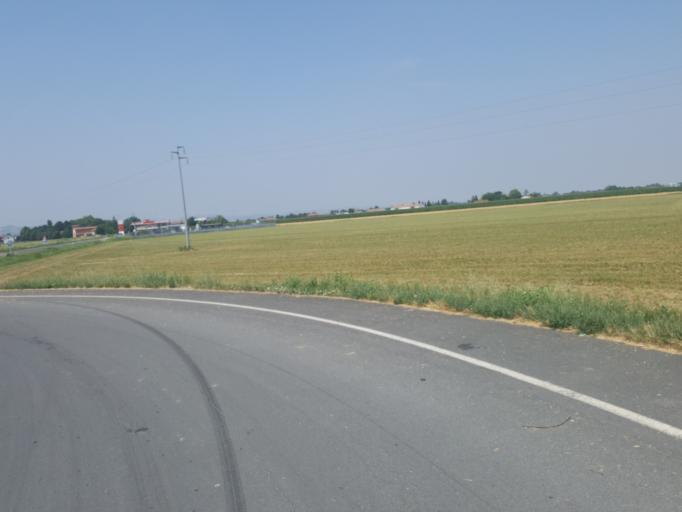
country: IT
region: Emilia-Romagna
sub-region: Provincia di Bologna
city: Castel San Pietro Terme
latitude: 44.4412
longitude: 11.6048
